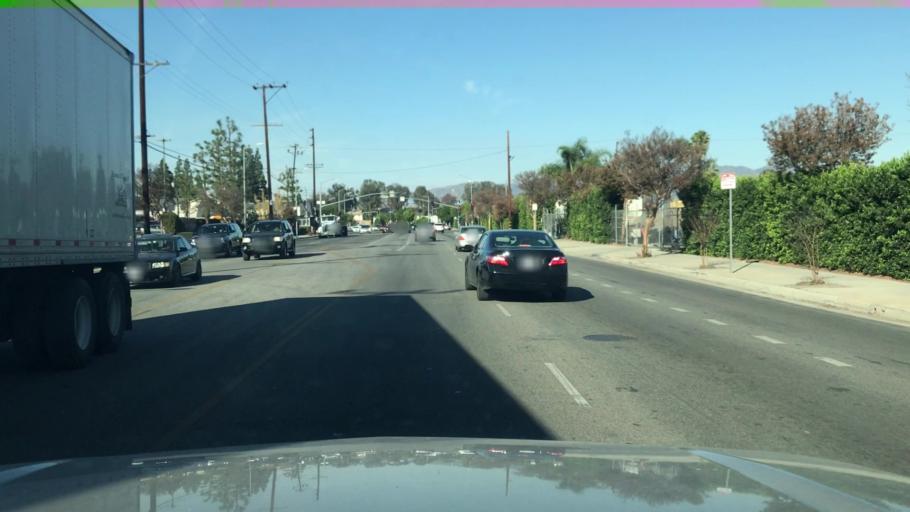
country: US
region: California
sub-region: Los Angeles County
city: Van Nuys
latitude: 34.2198
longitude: -118.4837
